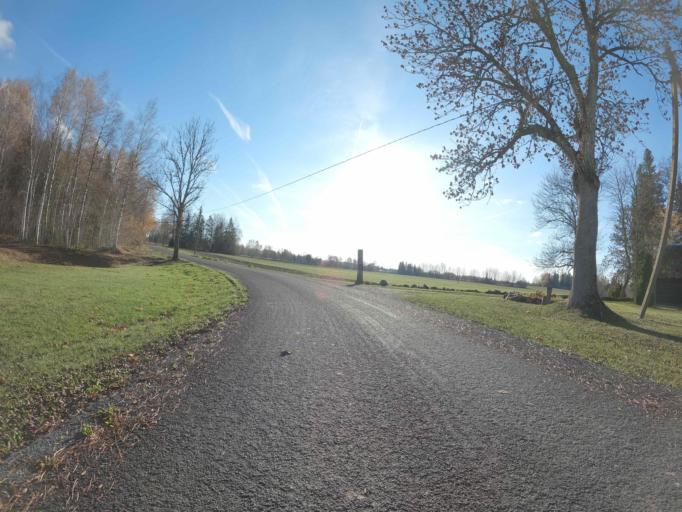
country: EE
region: Raplamaa
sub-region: Rapla vald
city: Rapla
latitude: 59.0197
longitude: 24.8012
